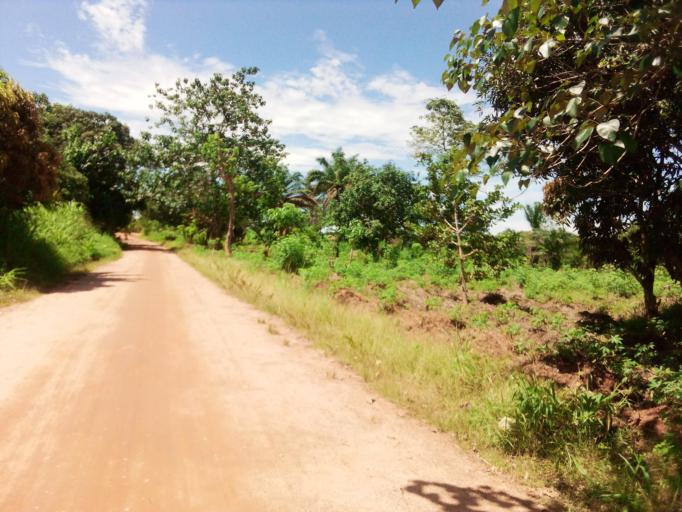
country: SL
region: Eastern Province
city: Koidu
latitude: 8.6557
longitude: -10.9452
